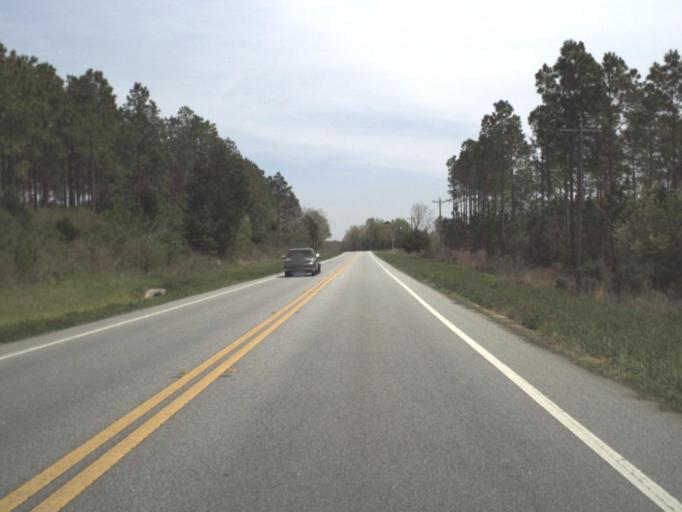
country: US
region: Alabama
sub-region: Geneva County
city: Geneva
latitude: 30.9459
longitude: -85.7611
